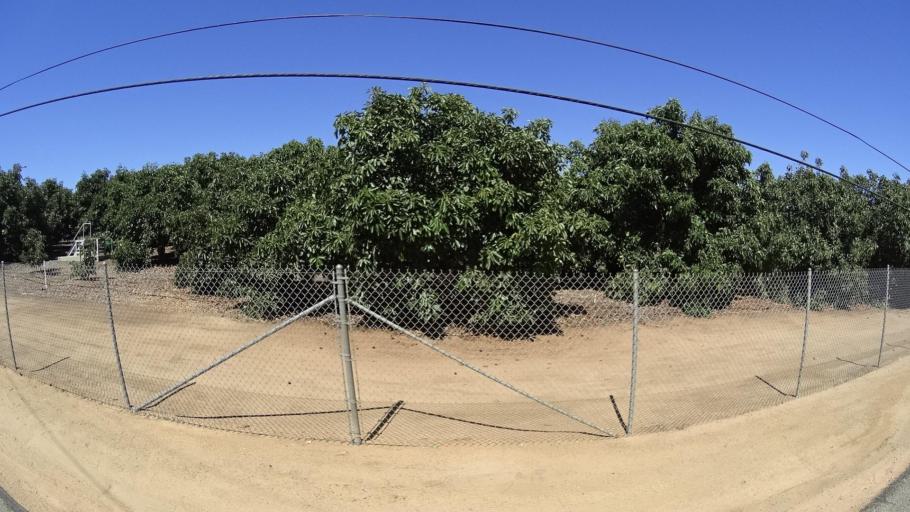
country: US
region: California
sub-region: San Diego County
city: Hidden Meadows
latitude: 33.2979
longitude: -117.1320
